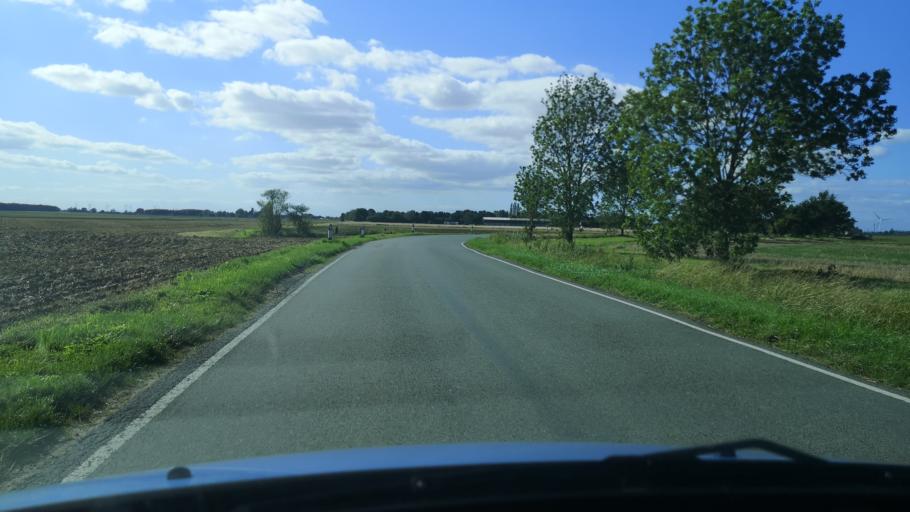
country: GB
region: England
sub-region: North Lincolnshire
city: Eastoft
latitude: 53.6340
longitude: -0.7636
